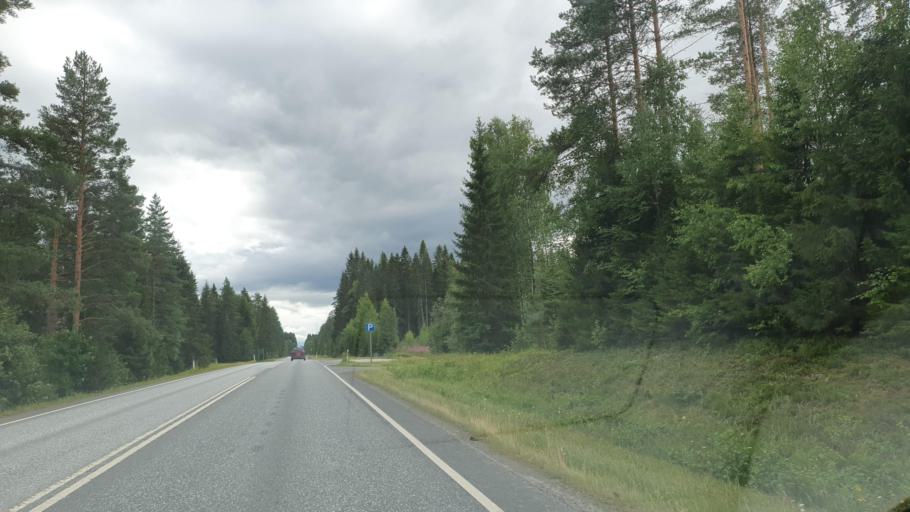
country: FI
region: Northern Savo
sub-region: Ylae-Savo
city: Sonkajaervi
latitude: 63.7946
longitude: 27.4186
